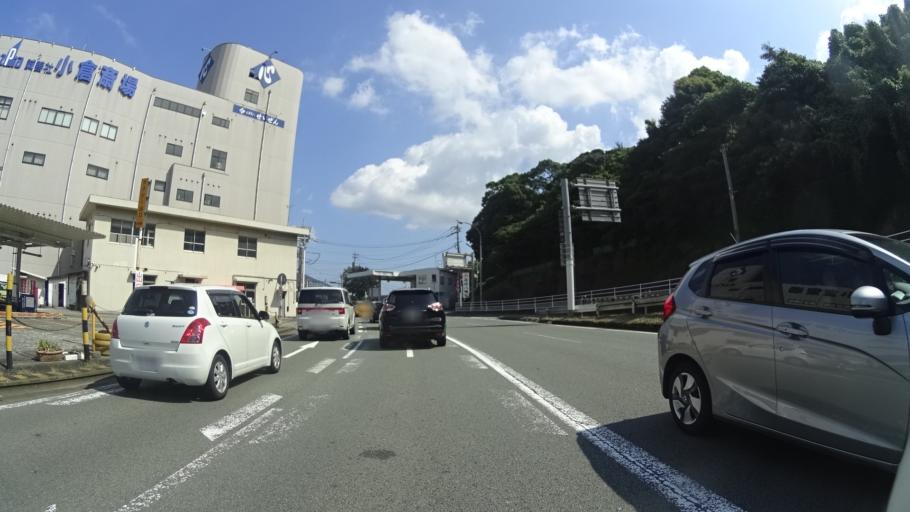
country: JP
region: Fukuoka
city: Kitakyushu
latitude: 33.8656
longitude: 130.8701
